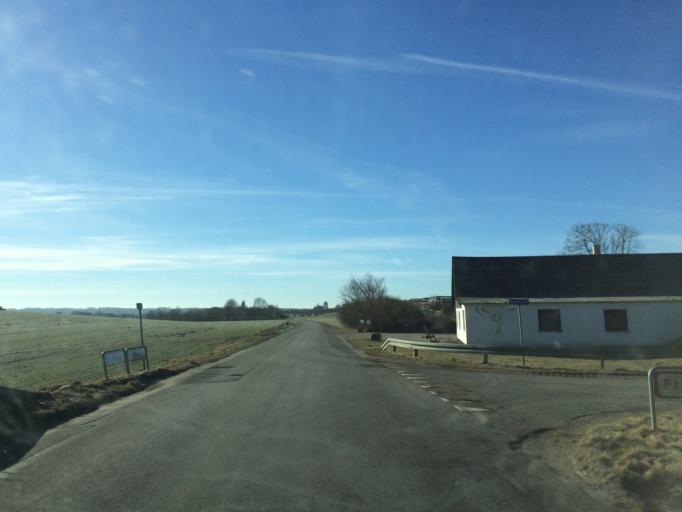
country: DK
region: North Denmark
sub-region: Mariagerfjord Kommune
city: Hobro
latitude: 56.6003
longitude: 9.6301
